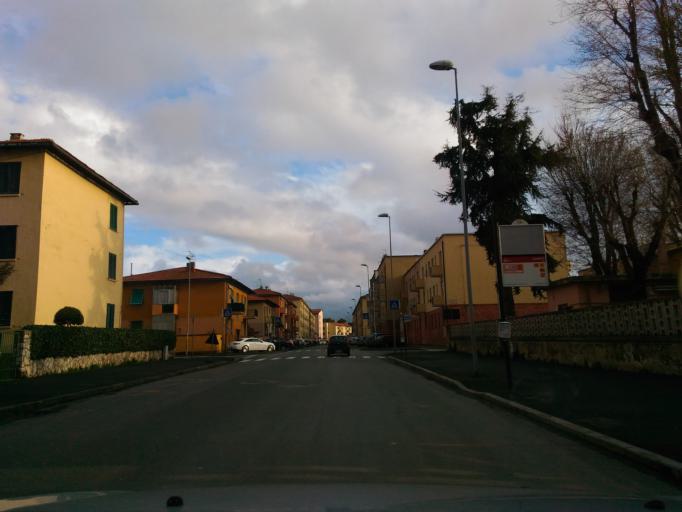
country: IT
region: Tuscany
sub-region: Provincia di Livorno
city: Livorno
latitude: 43.5629
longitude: 10.3308
